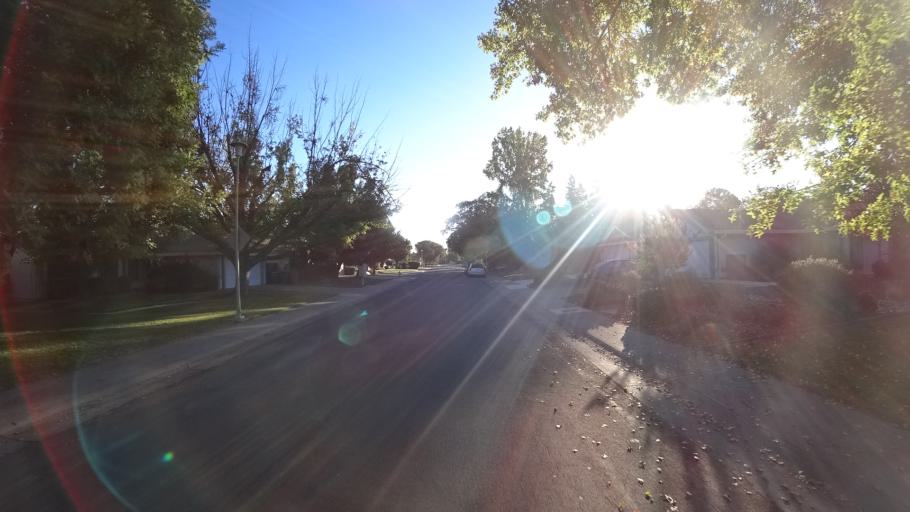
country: US
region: California
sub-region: Sacramento County
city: Parkway
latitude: 38.4939
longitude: -121.5455
